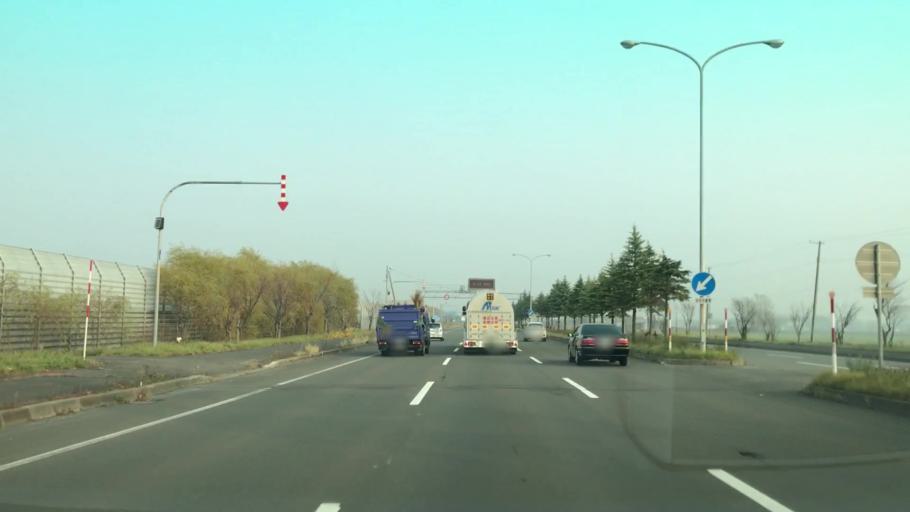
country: JP
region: Hokkaido
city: Ishikari
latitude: 43.1707
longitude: 141.3485
